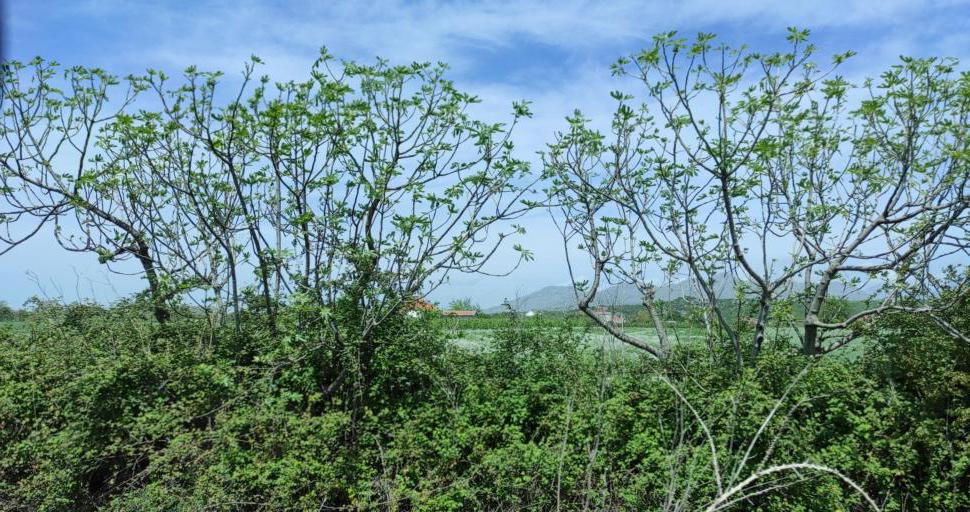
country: AL
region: Shkoder
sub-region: Rrethi i Malesia e Madhe
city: Gruemire
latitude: 42.1459
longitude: 19.5299
